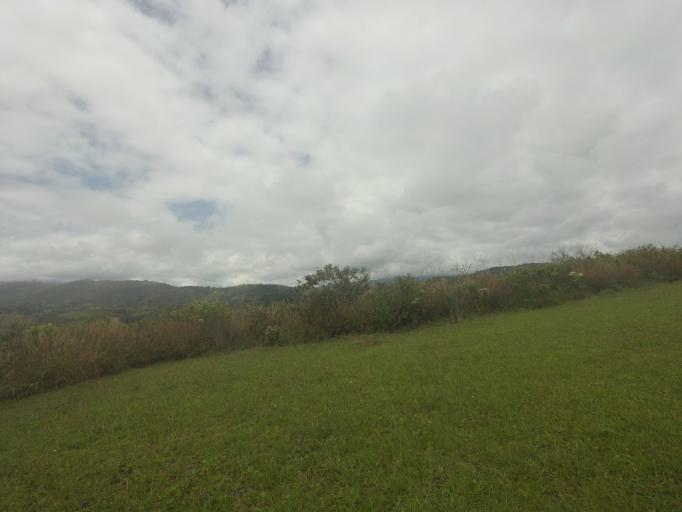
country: CO
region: Huila
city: San Agustin
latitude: 1.8801
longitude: -76.3034
